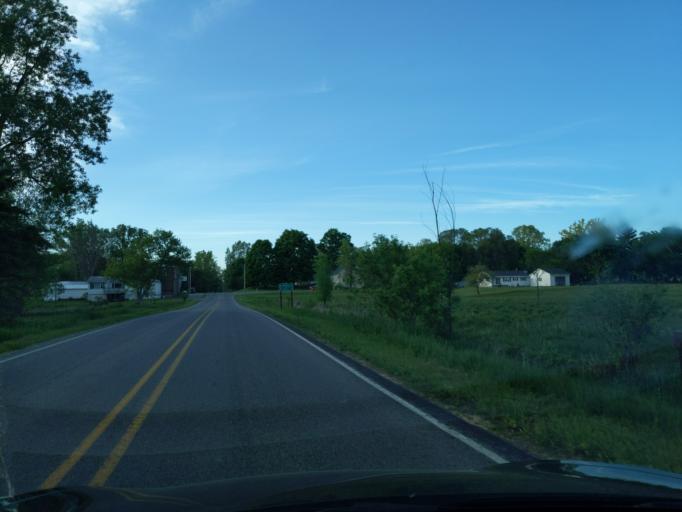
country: US
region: Michigan
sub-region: Ingham County
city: Leslie
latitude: 42.4737
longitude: -84.3170
